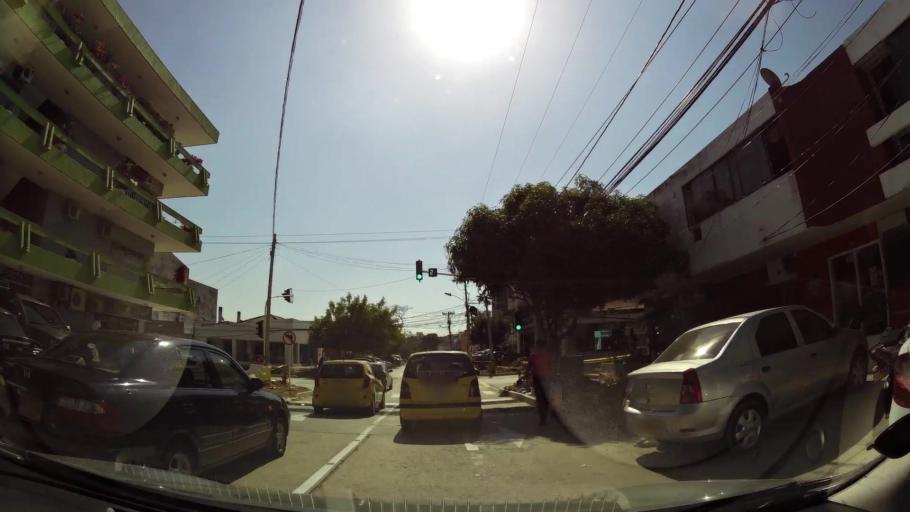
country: CO
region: Atlantico
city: Barranquilla
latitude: 10.9983
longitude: -74.8095
